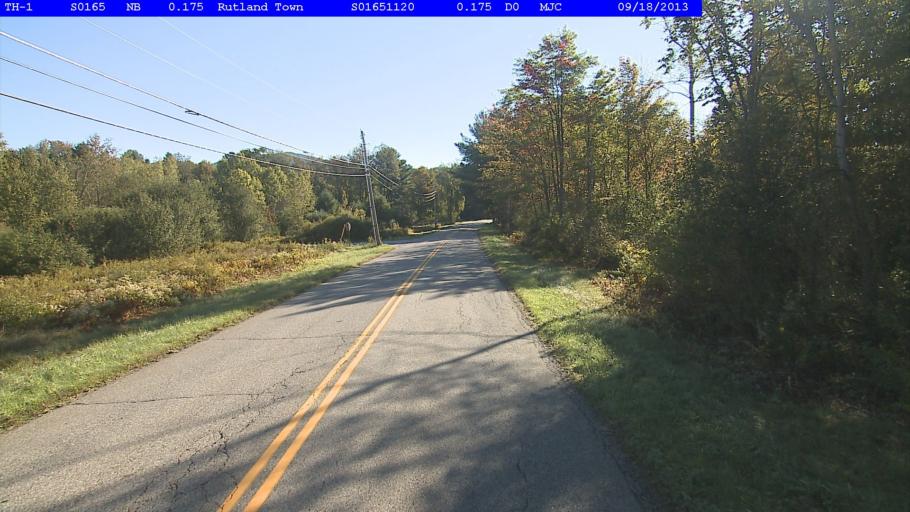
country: US
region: Vermont
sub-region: Rutland County
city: Rutland
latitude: 43.6523
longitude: -72.9688
